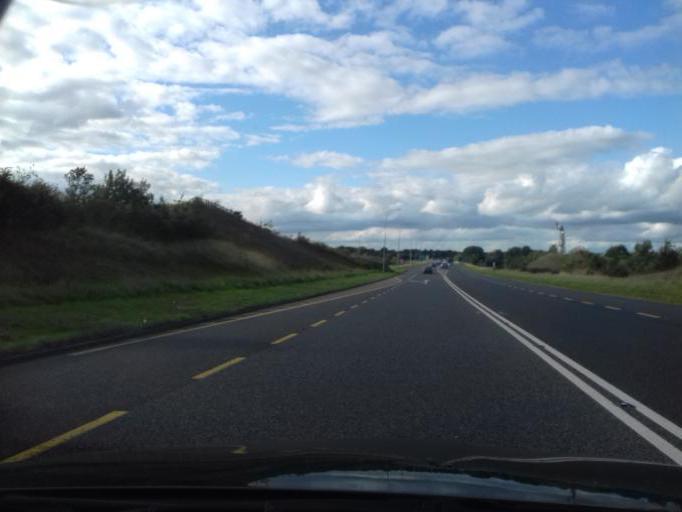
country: IE
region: Leinster
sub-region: Uibh Fhaili
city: Tullamore
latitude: 53.3020
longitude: -7.4881
